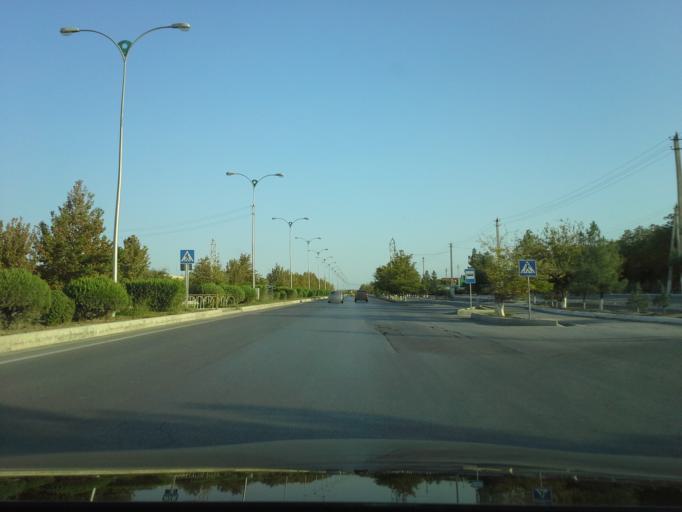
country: TM
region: Ahal
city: Abadan
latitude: 38.0303
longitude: 58.1938
